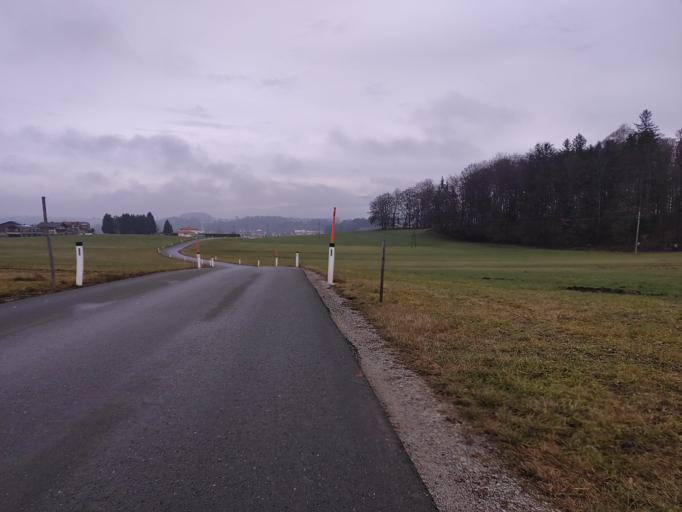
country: AT
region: Salzburg
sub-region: Politischer Bezirk Salzburg-Umgebung
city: Seekirchen am Wallersee
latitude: 47.8946
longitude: 13.1450
